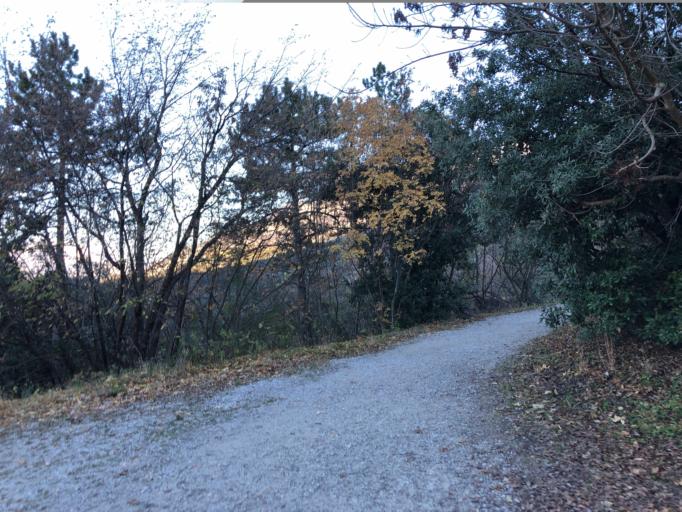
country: IT
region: Trentino-Alto Adige
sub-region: Provincia di Trento
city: Torbole sul Garda
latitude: 45.8609
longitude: 10.8801
